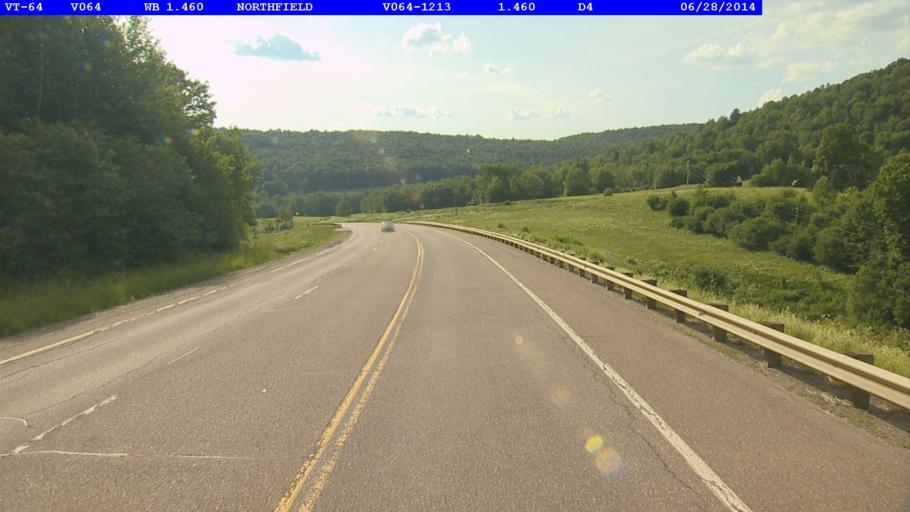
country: US
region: Vermont
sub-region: Washington County
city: Northfield
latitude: 44.1207
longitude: -72.6311
